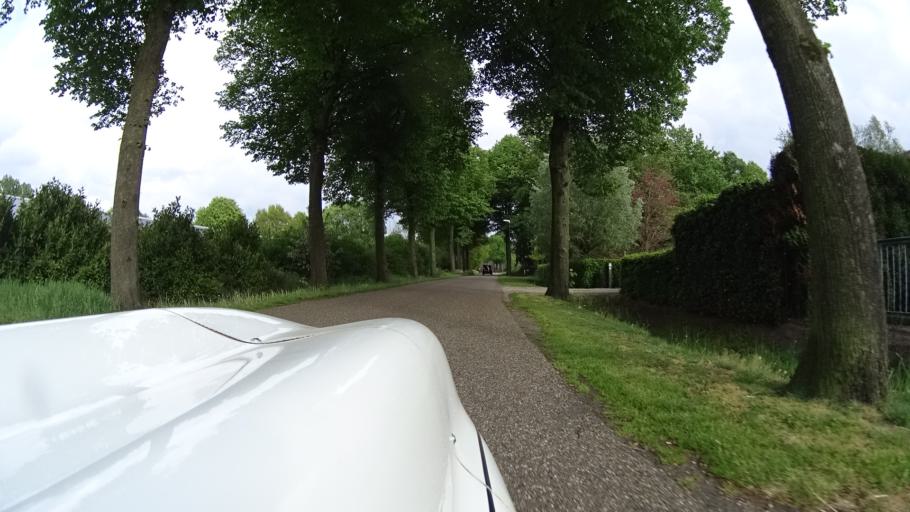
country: NL
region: North Brabant
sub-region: Gemeente Uden
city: Volkel
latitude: 51.6341
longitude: 5.6707
